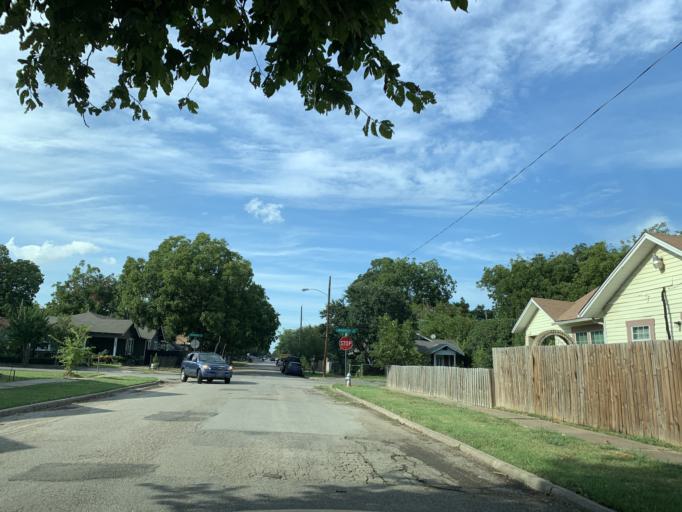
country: US
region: Texas
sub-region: Dallas County
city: Dallas
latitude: 32.7389
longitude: -96.8340
